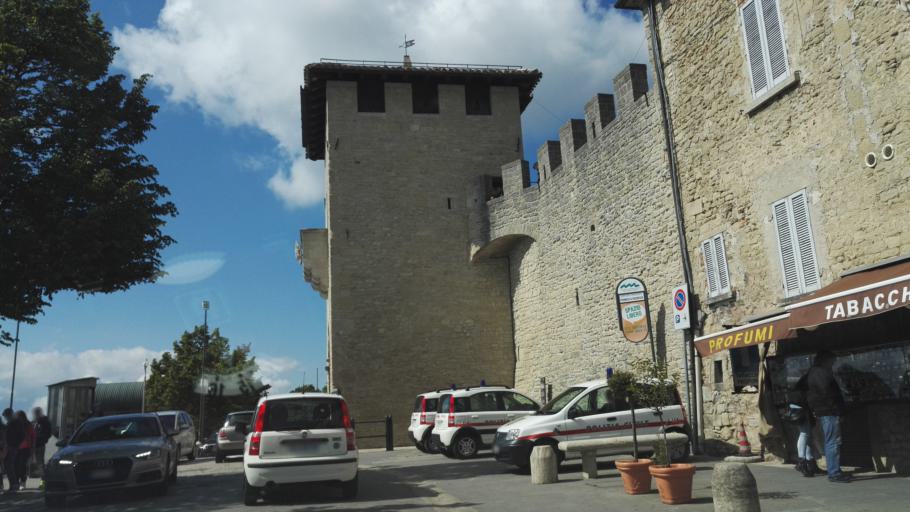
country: SM
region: San Marino
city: San Marino
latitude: 43.9350
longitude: 12.4470
